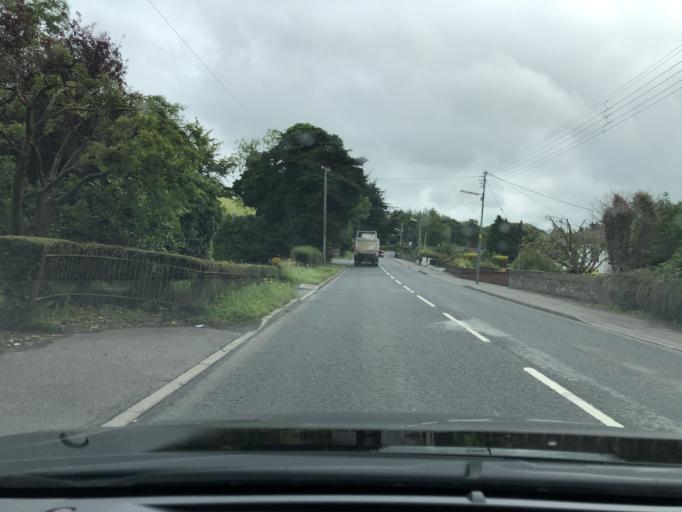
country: GB
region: Northern Ireland
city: Ballynahinch
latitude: 54.3981
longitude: -5.8944
